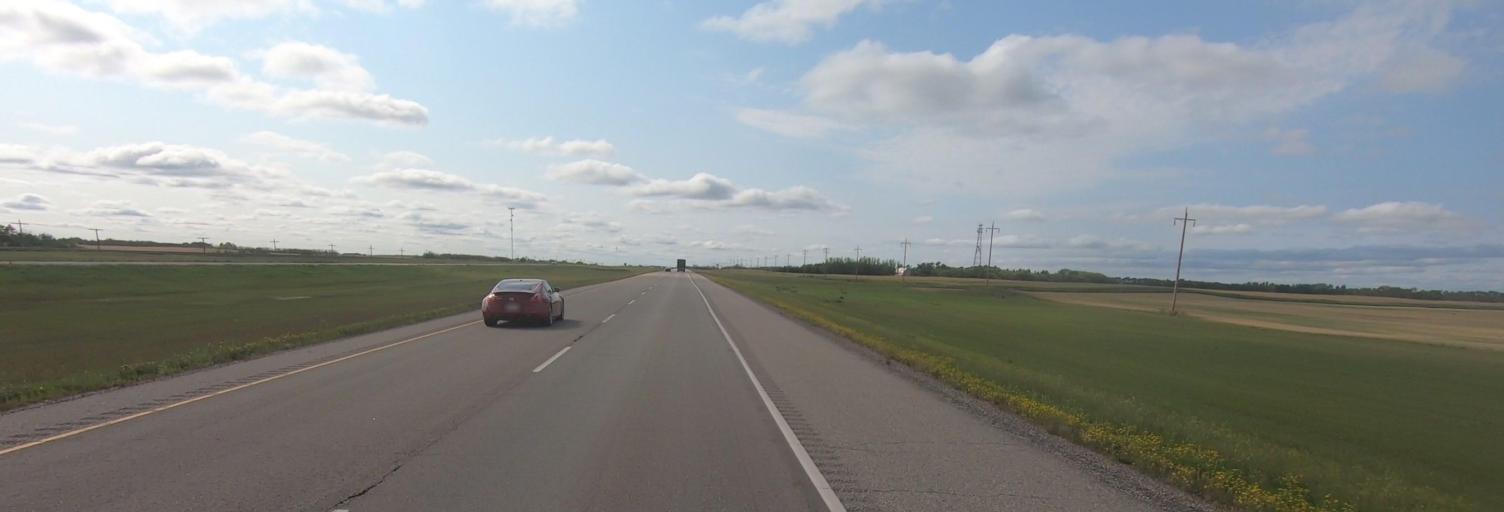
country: CA
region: Manitoba
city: Virden
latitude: 49.9415
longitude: -101.1344
